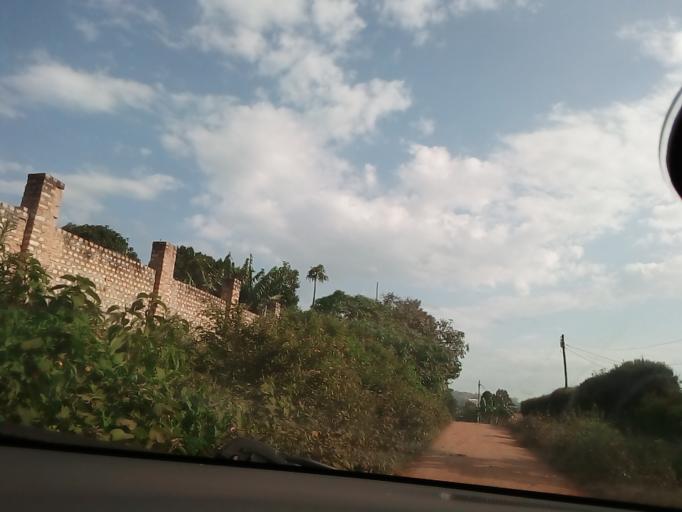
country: UG
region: Central Region
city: Masaka
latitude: -0.3516
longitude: 31.7442
